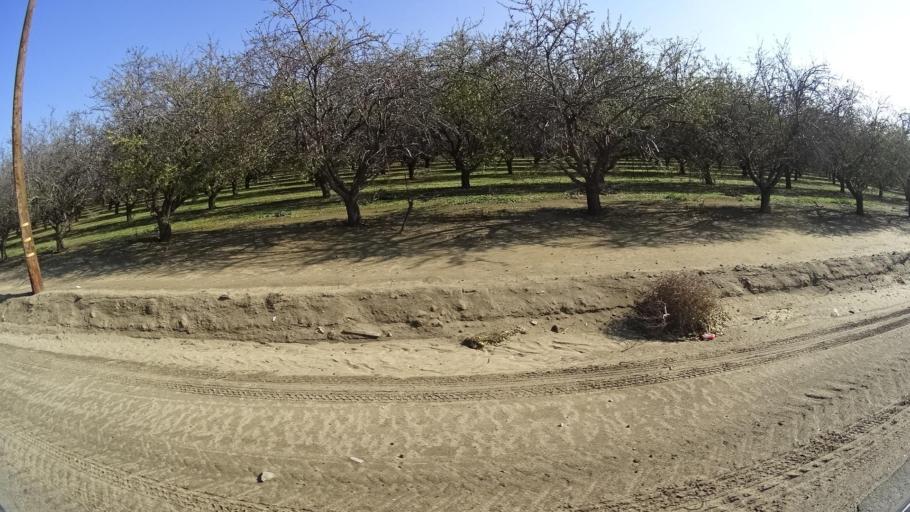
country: US
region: California
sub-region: Kern County
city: Arvin
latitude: 35.2349
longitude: -118.8066
